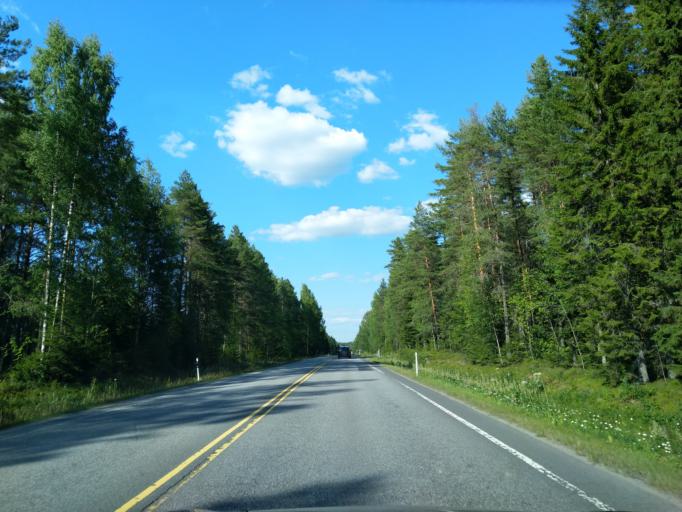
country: FI
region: Pirkanmaa
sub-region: Luoteis-Pirkanmaa
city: Kihnioe
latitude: 62.1438
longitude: 23.1487
